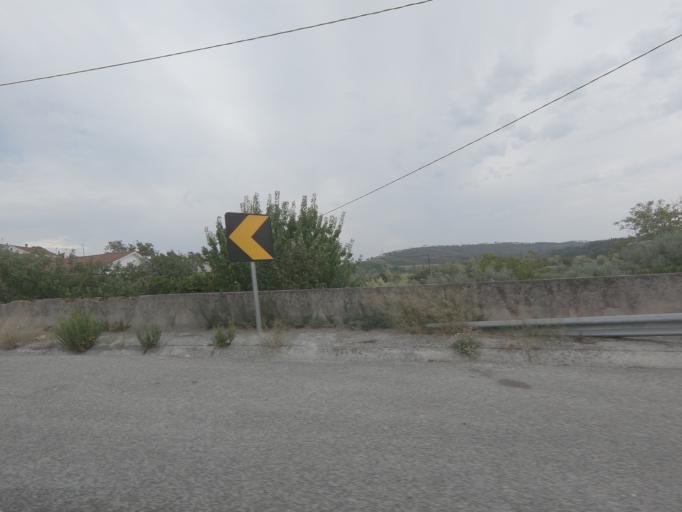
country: PT
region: Coimbra
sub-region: Condeixa-A-Nova
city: Condeixa-a-Nova
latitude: 40.1320
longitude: -8.4755
